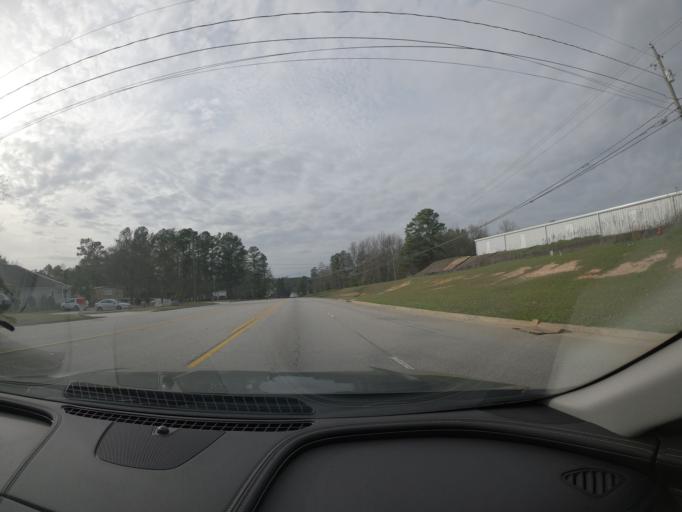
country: US
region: Georgia
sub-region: Columbia County
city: Evans
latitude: 33.4748
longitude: -82.1314
